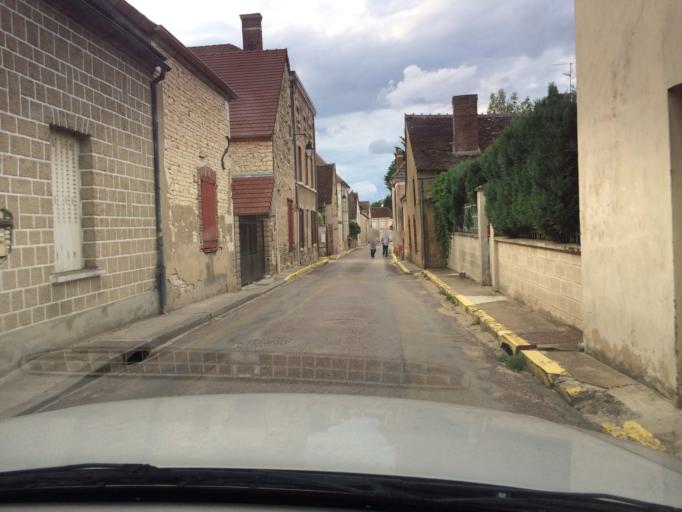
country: FR
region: Bourgogne
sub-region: Departement de l'Yonne
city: Fleury-la-Vallee
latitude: 47.8706
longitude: 3.4527
